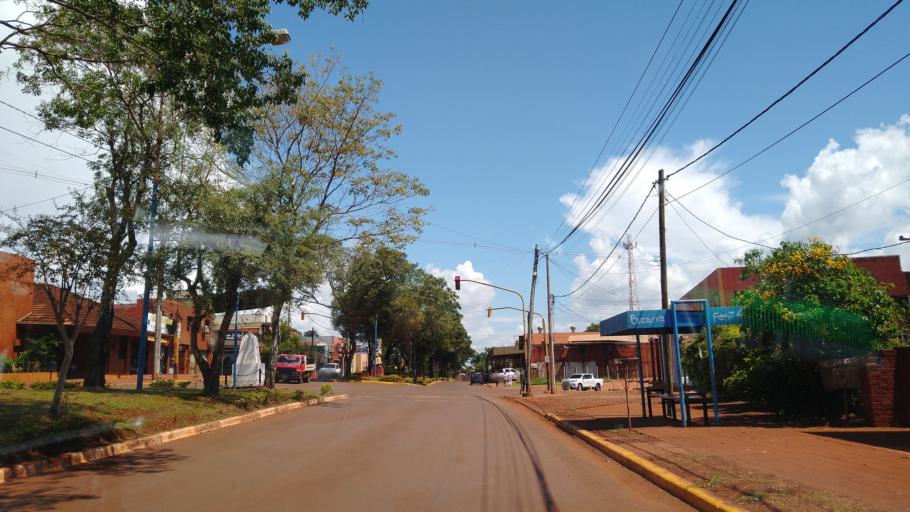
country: AR
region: Misiones
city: Puerto Libertad
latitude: -25.9724
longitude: -54.5640
